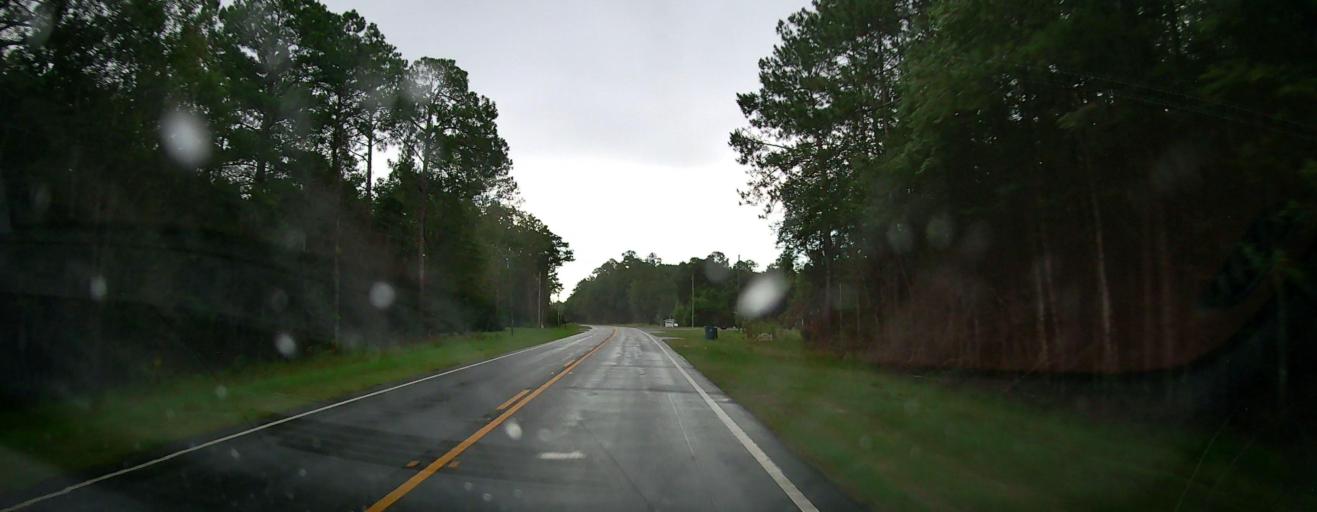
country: US
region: Georgia
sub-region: Glynn County
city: Dock Junction
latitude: 31.3171
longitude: -81.7468
